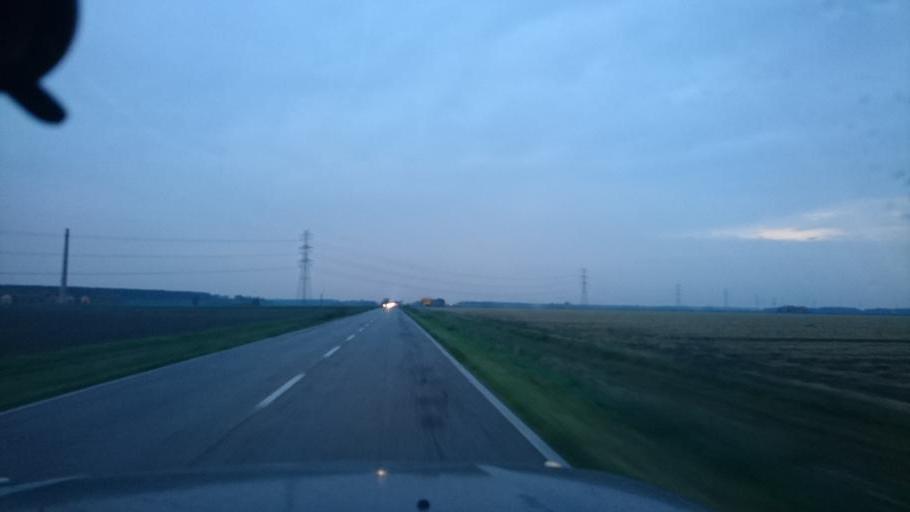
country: IT
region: Veneto
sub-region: Provincia di Rovigo
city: Porto Tolle
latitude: 44.9479
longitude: 12.2868
